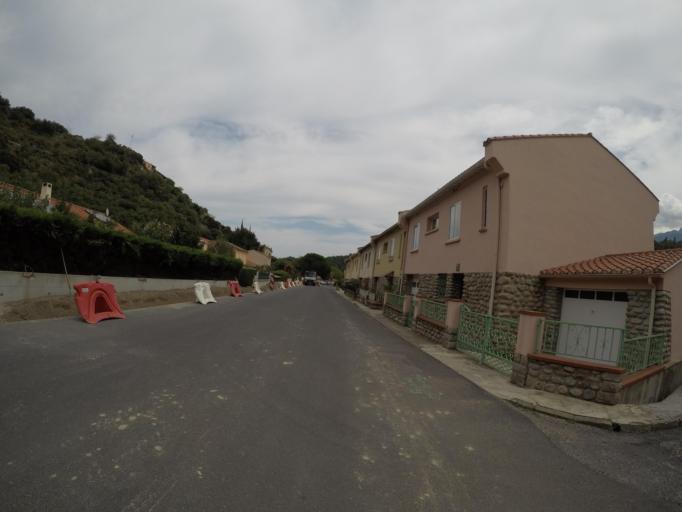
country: FR
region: Languedoc-Roussillon
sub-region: Departement des Pyrenees-Orientales
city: Ria-Sirach
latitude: 42.6075
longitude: 2.3949
